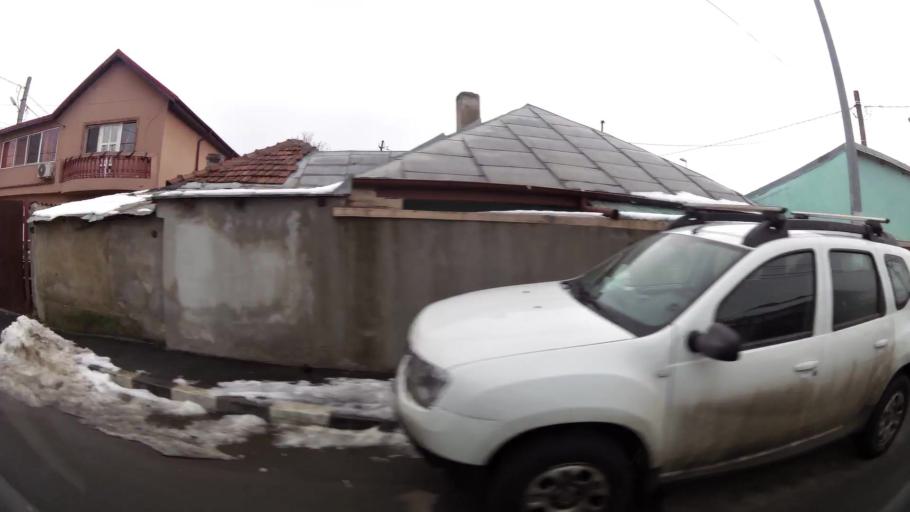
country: RO
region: Ilfov
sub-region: Comuna Pantelimon
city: Pantelimon
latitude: 44.4592
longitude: 26.2018
